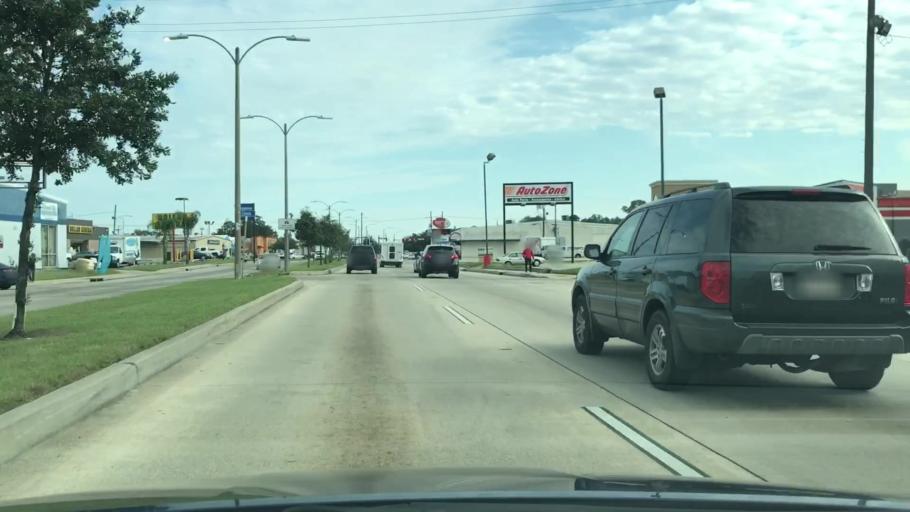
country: US
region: Louisiana
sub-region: Jefferson Parish
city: Jefferson
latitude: 29.9626
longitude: -90.1173
